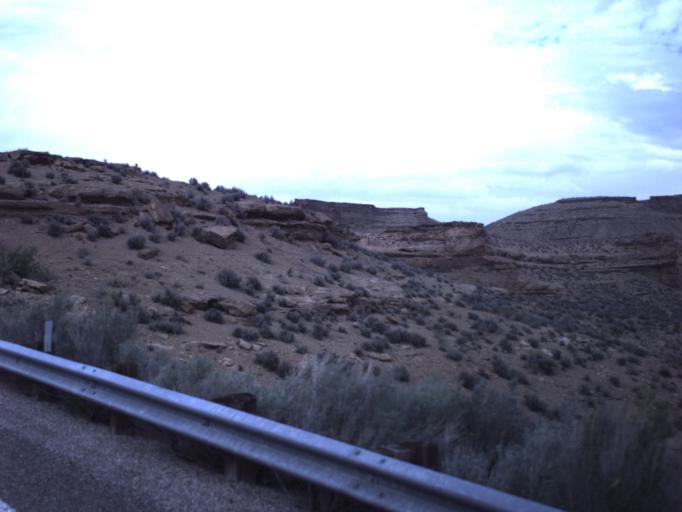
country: US
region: Colorado
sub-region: Rio Blanco County
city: Rangely
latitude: 39.9905
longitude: -109.1772
